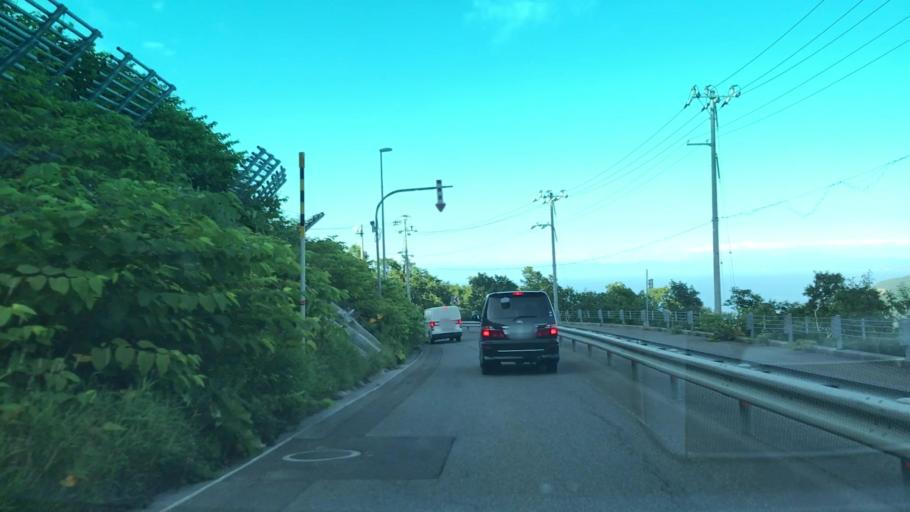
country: JP
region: Hokkaido
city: Otaru
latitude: 43.1390
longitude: 141.0144
